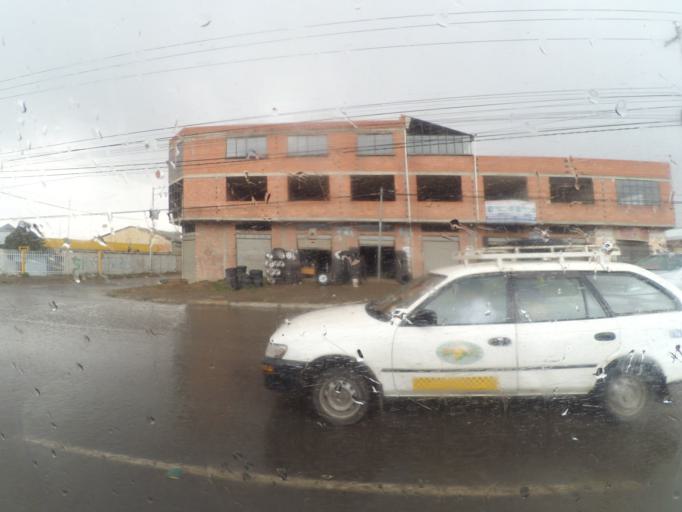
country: BO
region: La Paz
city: La Paz
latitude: -16.5347
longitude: -68.1731
